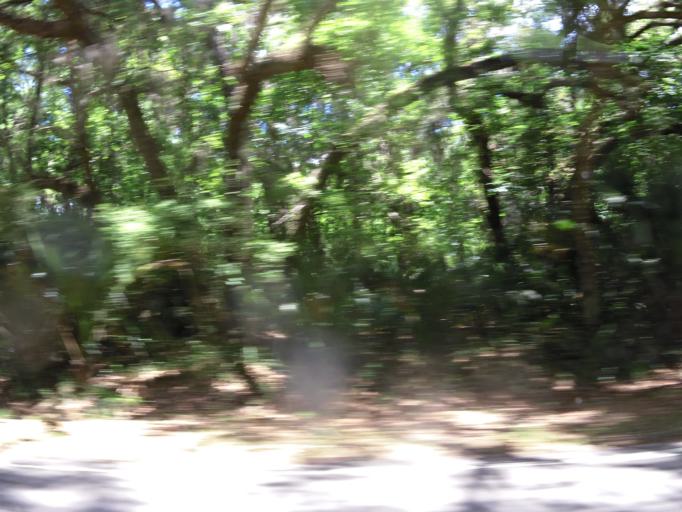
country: US
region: Florida
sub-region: Duval County
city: Atlantic Beach
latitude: 30.4465
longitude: -81.4642
